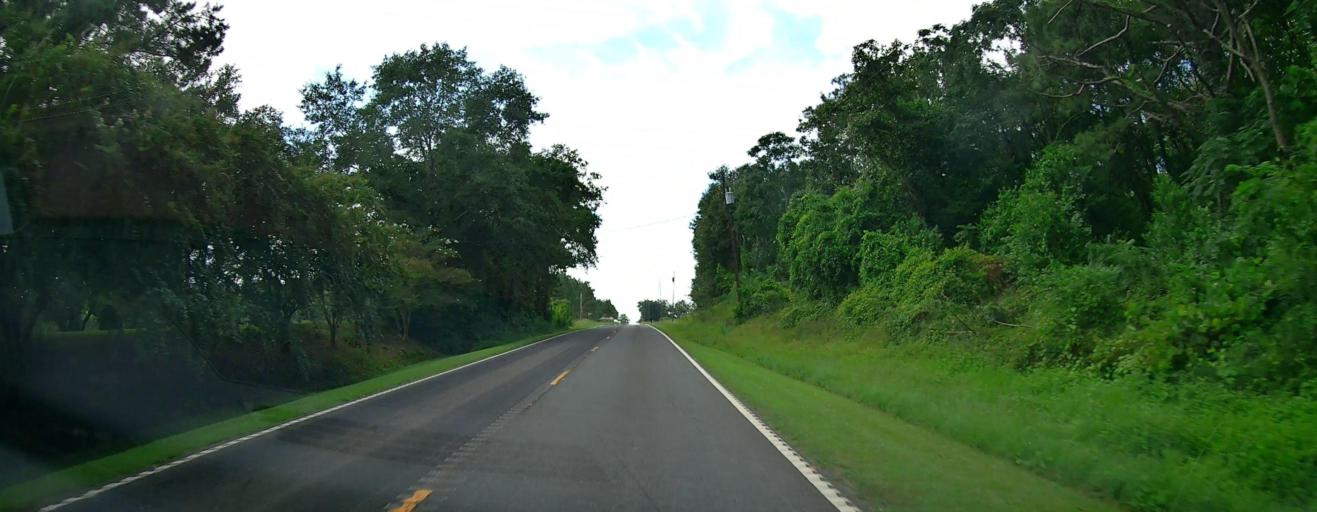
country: US
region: Georgia
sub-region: Taylor County
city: Reynolds
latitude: 32.4402
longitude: -84.1263
